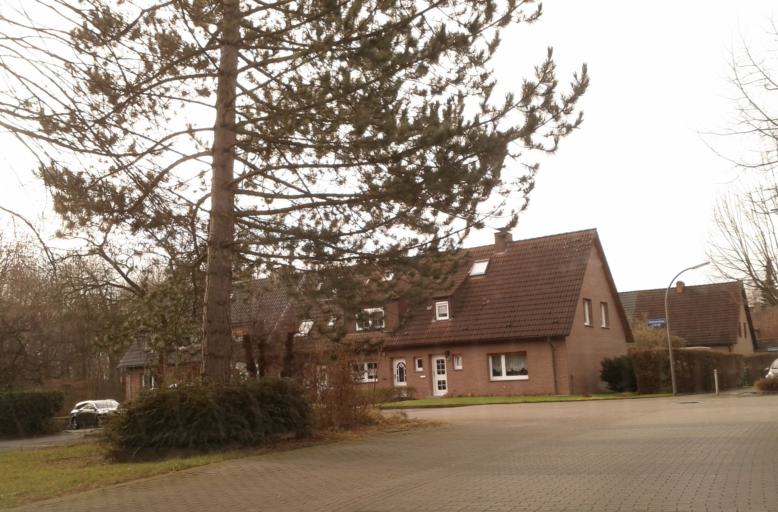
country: DE
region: North Rhine-Westphalia
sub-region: Regierungsbezirk Arnsberg
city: Dortmund
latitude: 51.5525
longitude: 7.5050
